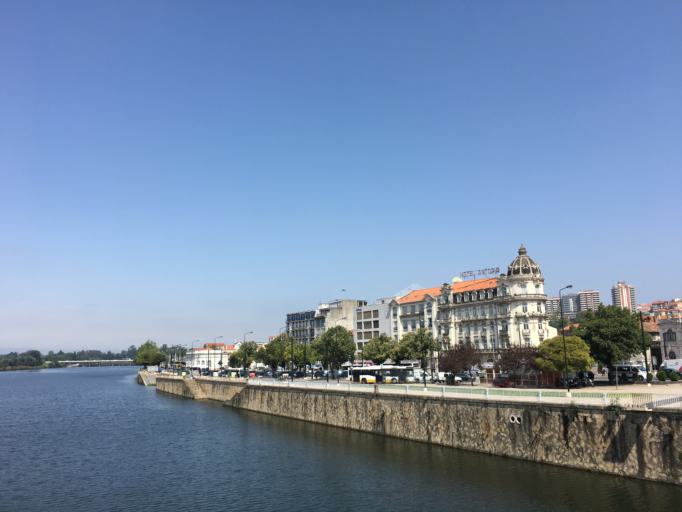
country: PT
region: Coimbra
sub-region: Coimbra
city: Coimbra
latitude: 40.2065
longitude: -8.4302
